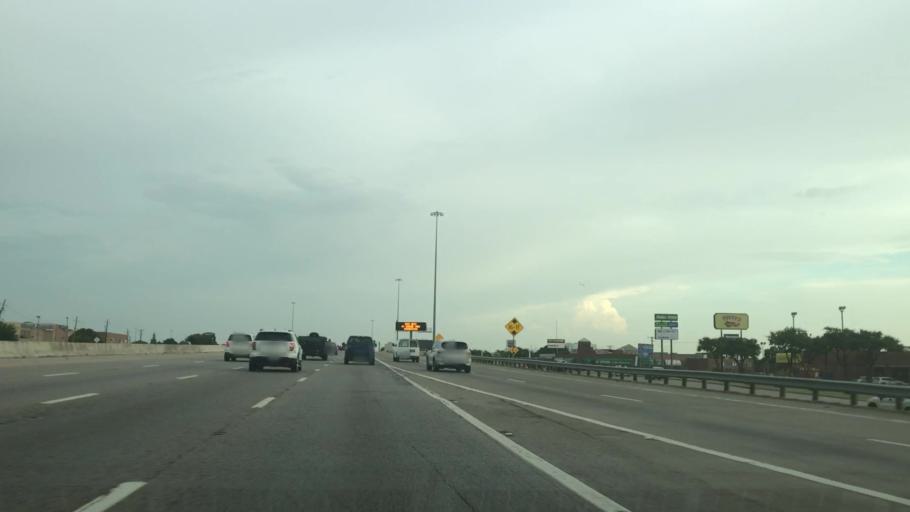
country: US
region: Texas
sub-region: Dallas County
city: Mesquite
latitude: 32.8138
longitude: -96.6284
